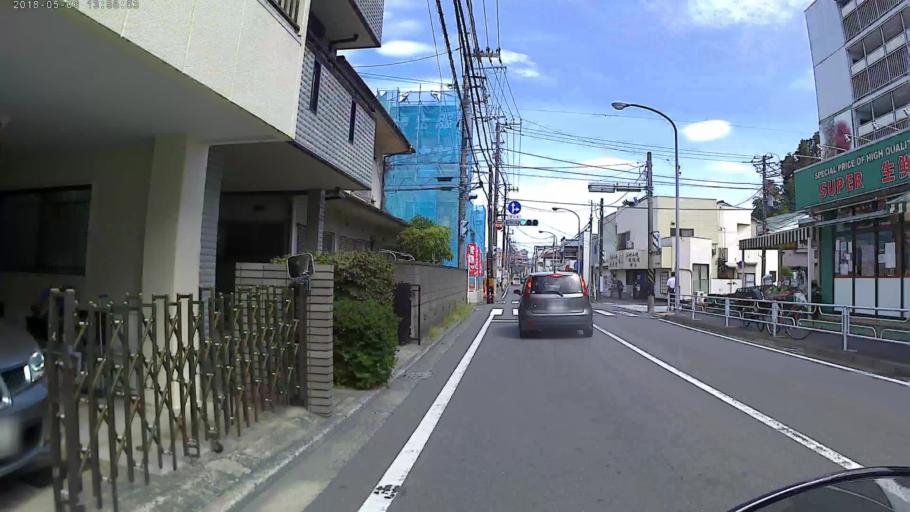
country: JP
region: Kanagawa
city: Yokohama
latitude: 35.4384
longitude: 139.5936
